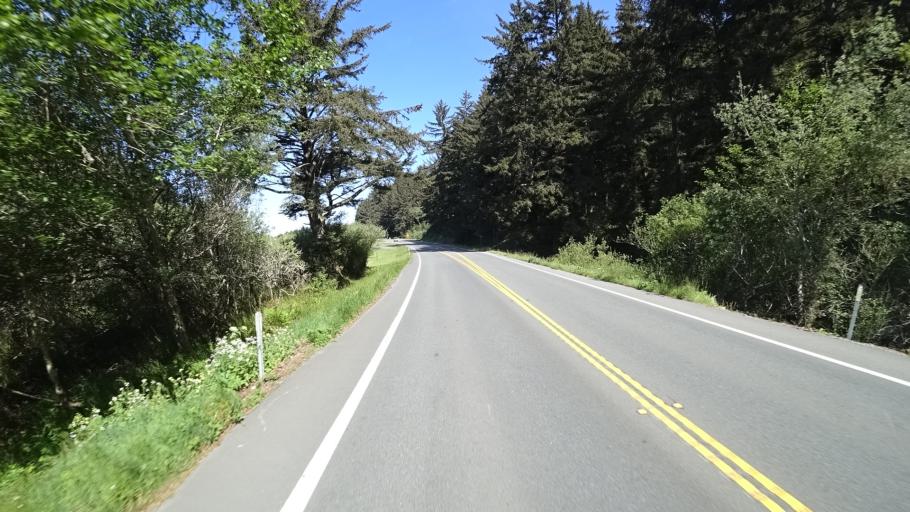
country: US
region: California
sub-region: Del Norte County
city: Bertsch-Oceanview
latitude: 41.5927
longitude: -124.0972
